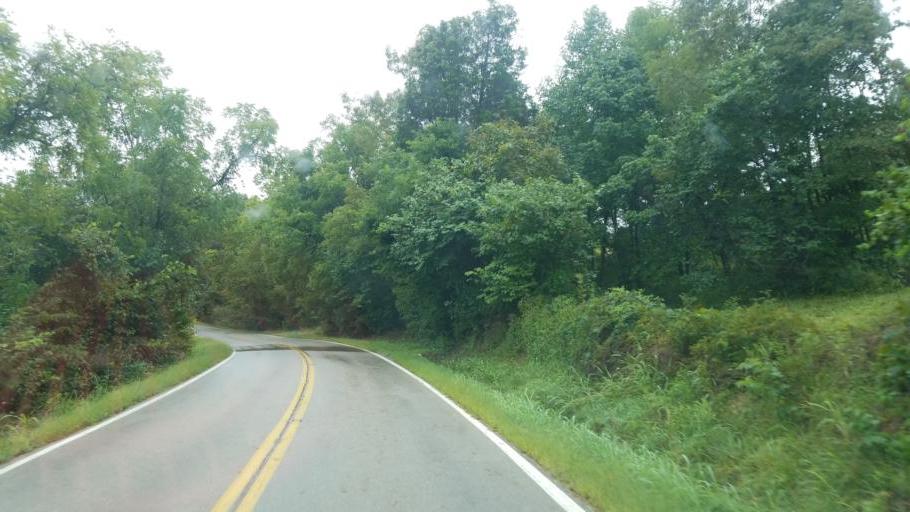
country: US
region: Ohio
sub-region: Adams County
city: West Union
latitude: 38.7215
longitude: -83.5124
